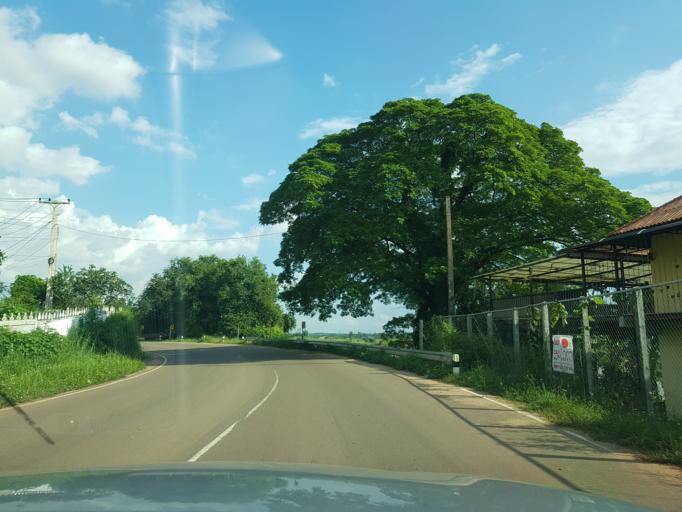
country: TH
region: Nong Khai
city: Pho Tak
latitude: 17.9777
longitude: 102.4660
